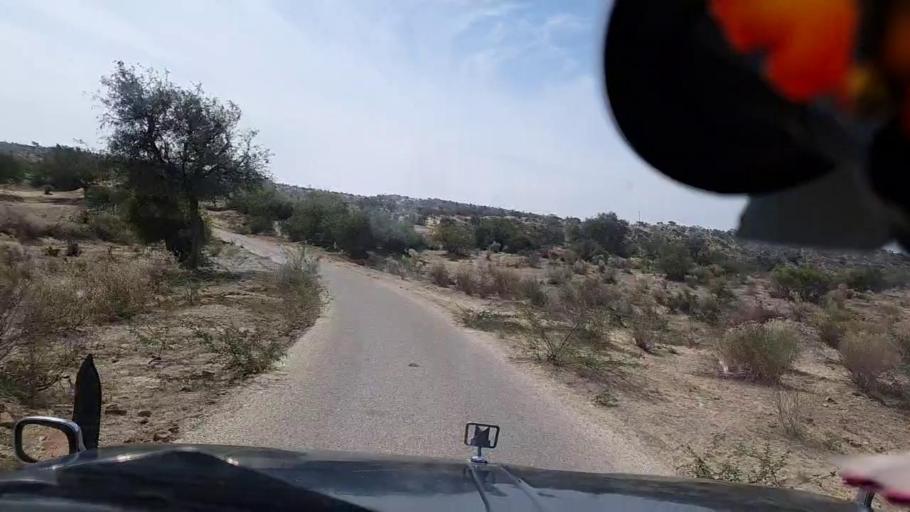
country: PK
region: Sindh
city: Diplo
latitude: 24.3933
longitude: 69.5880
